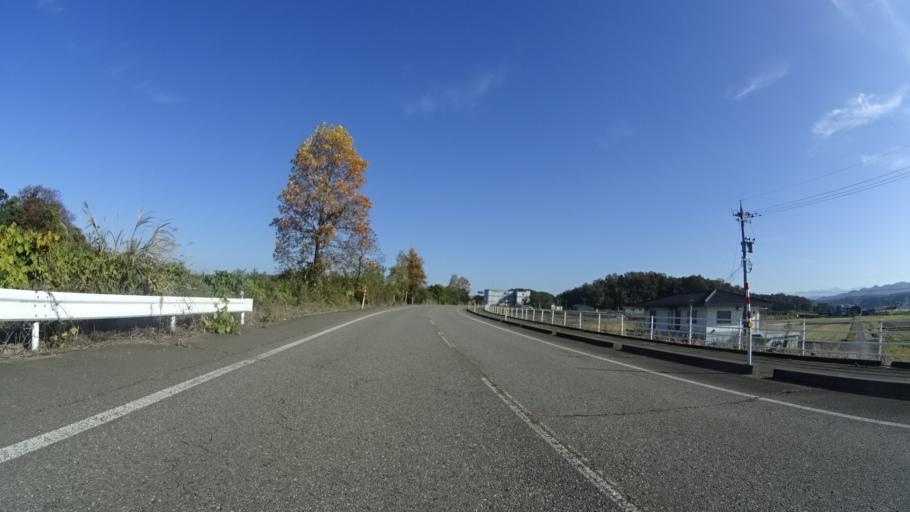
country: JP
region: Ishikawa
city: Komatsu
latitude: 36.3098
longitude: 136.3860
